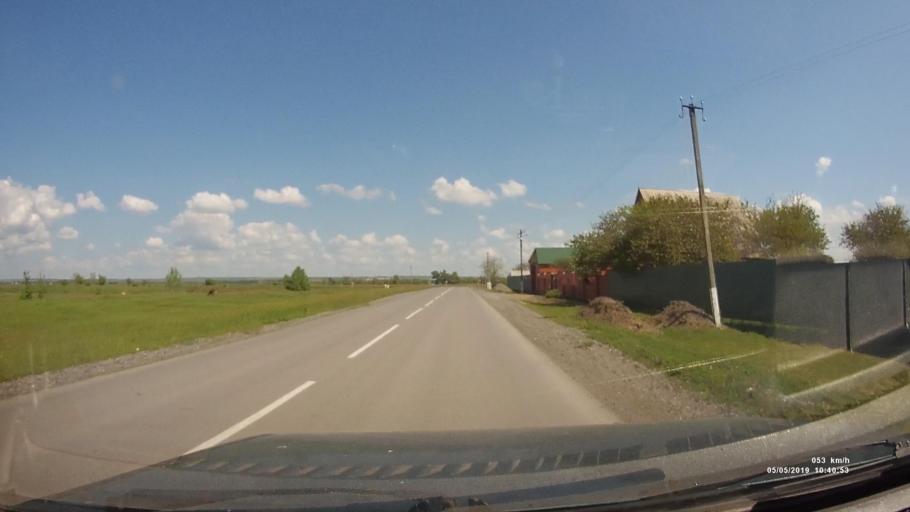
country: RU
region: Rostov
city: Ust'-Donetskiy
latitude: 47.5875
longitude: 40.8425
